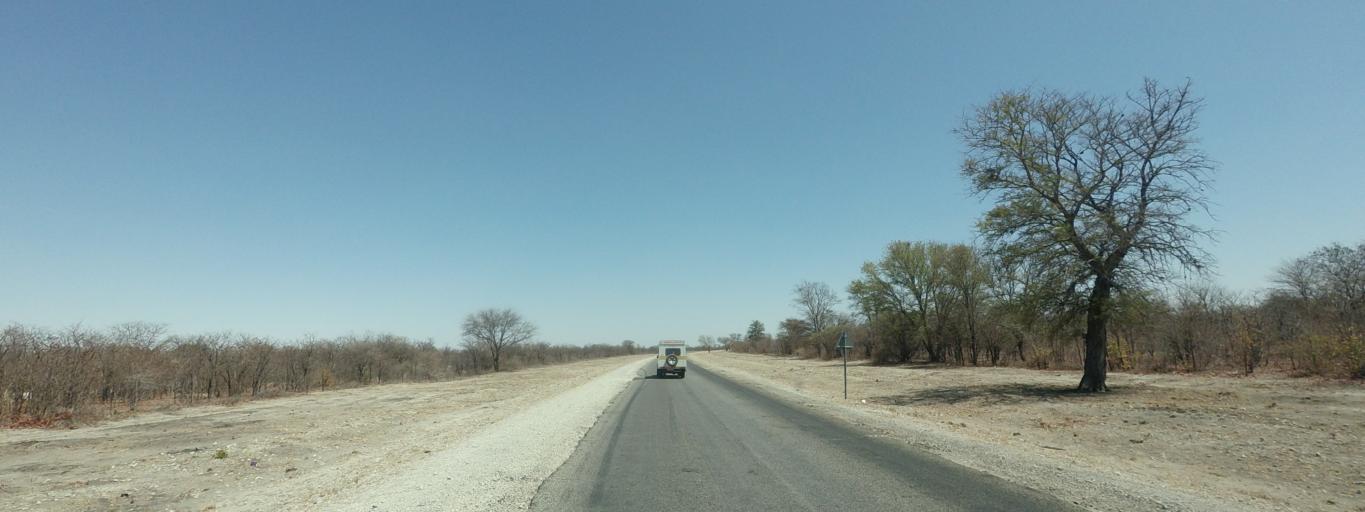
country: BW
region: North East
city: Dukwe
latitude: -20.3831
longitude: 26.3308
